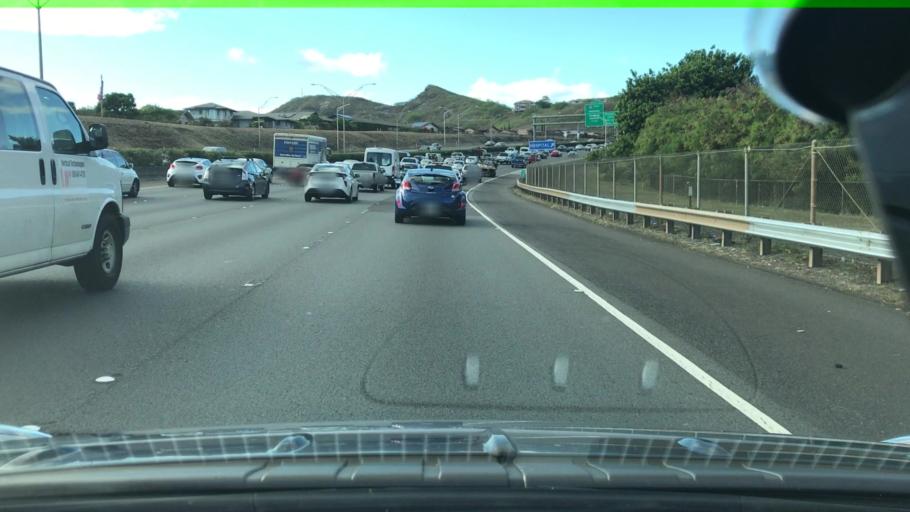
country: US
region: Hawaii
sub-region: Honolulu County
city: Halawa Heights
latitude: 21.3558
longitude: -157.8979
